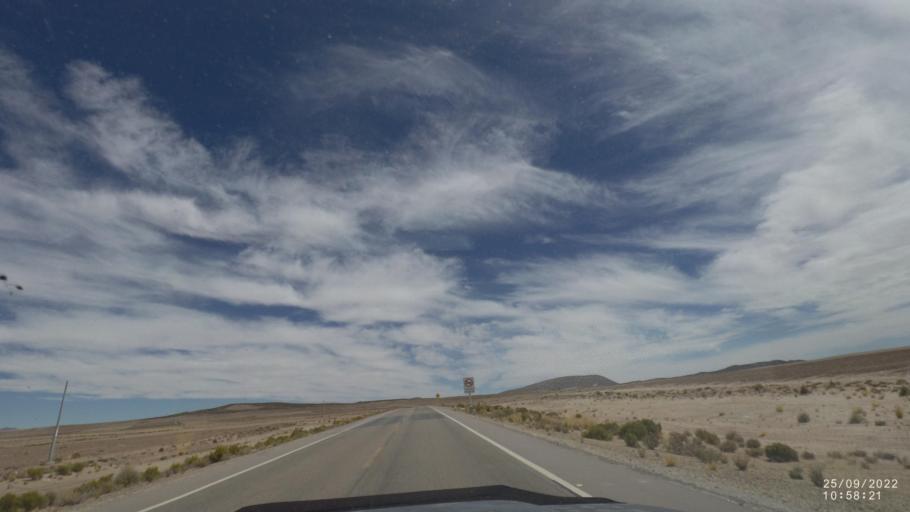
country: BO
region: Oruro
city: Challapata
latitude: -19.4650
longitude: -66.9052
